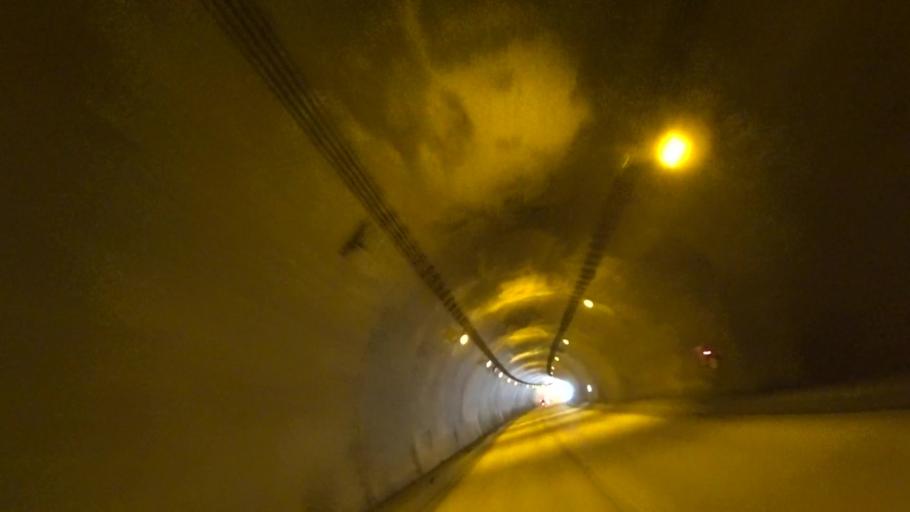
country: JP
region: Kyoto
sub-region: Kyoto-shi
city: Kamigyo-ku
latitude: 35.0835
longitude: 135.6870
